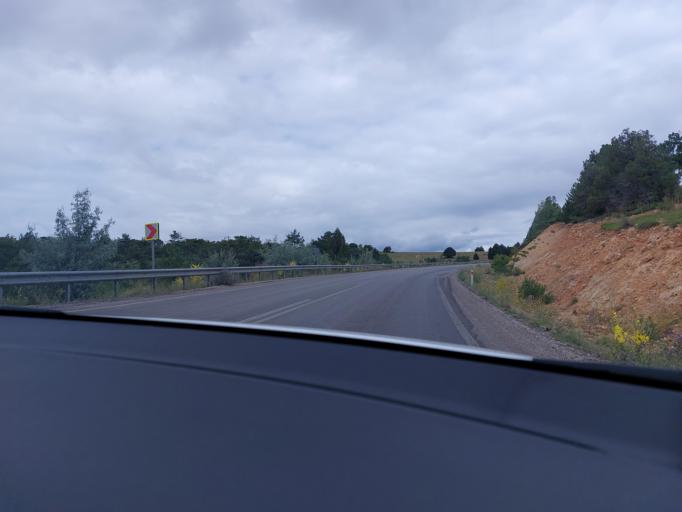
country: TR
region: Konya
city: Doganbey
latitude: 37.8923
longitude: 31.8171
